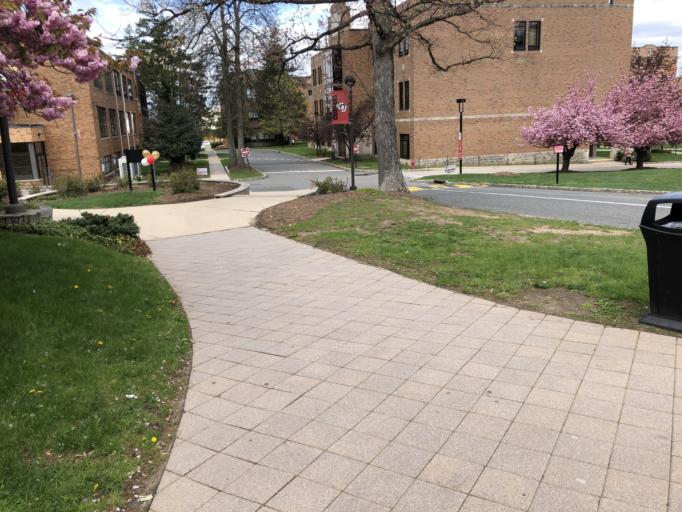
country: US
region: New Jersey
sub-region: Essex County
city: Caldwell
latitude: 40.8330
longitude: -74.2722
